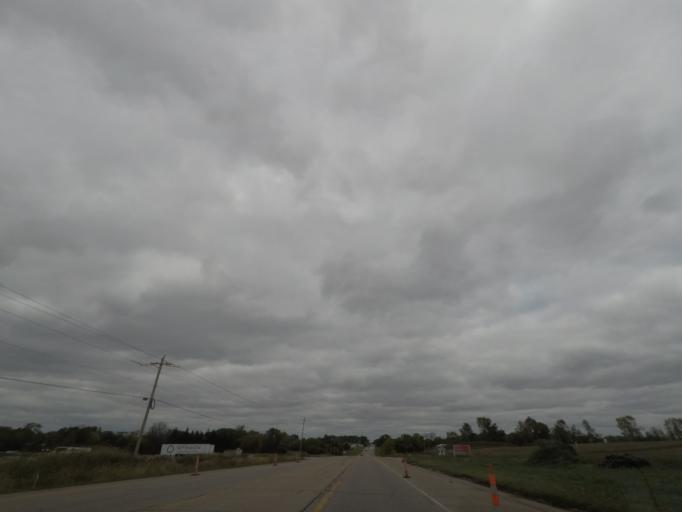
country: US
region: Iowa
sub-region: Polk County
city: Saylorville
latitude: 41.6821
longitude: -93.6005
